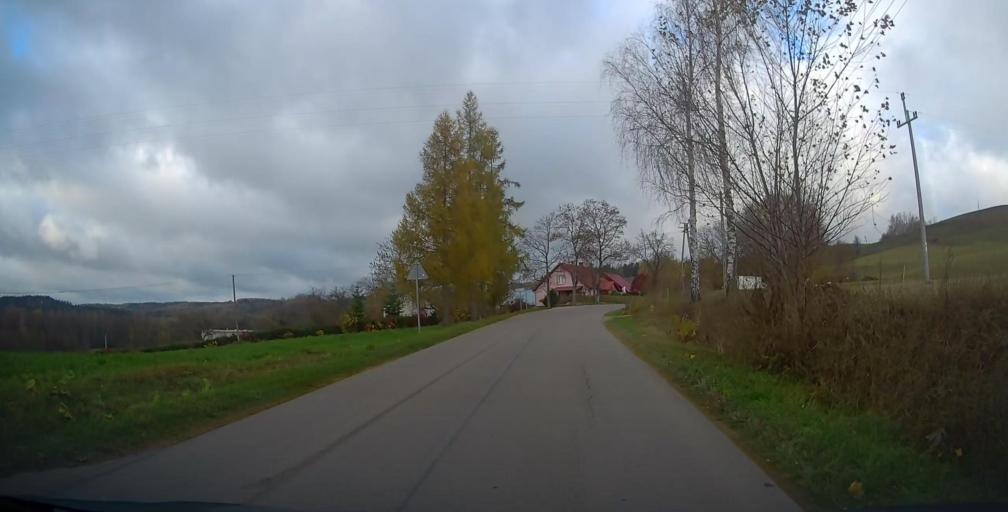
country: PL
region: Podlasie
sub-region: Suwalki
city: Suwalki
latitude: 54.2820
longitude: 22.9058
